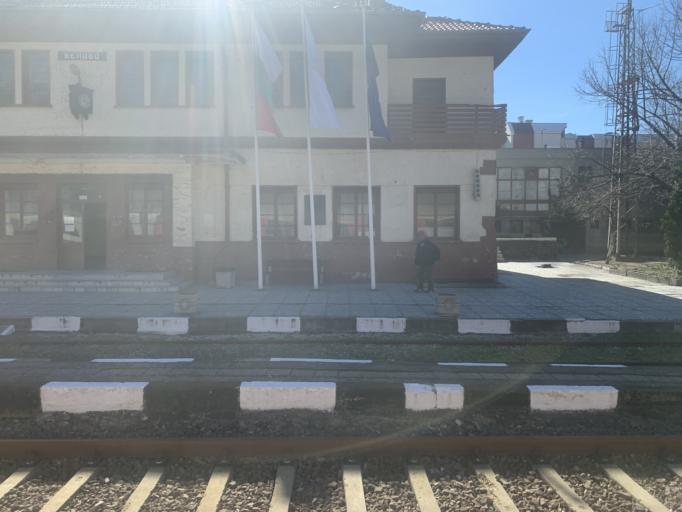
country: BG
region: Pazardzhik
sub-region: Obshtina Belovo
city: Belovo
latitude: 42.2157
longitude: 24.0183
